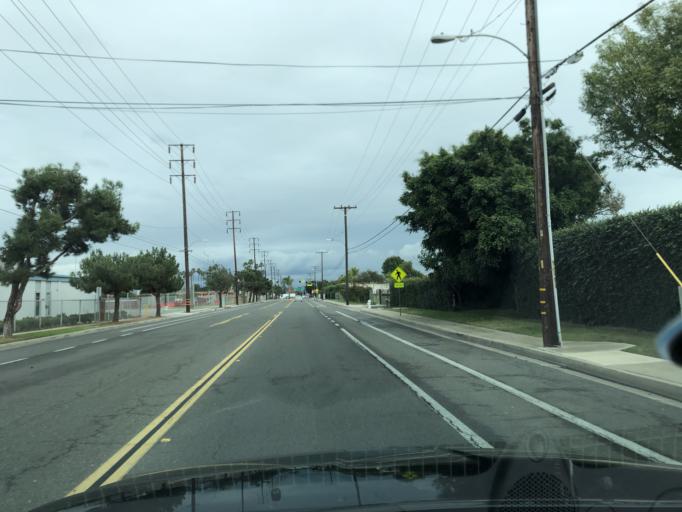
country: US
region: California
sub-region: Orange County
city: Fountain Valley
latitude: 33.6870
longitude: -117.9250
